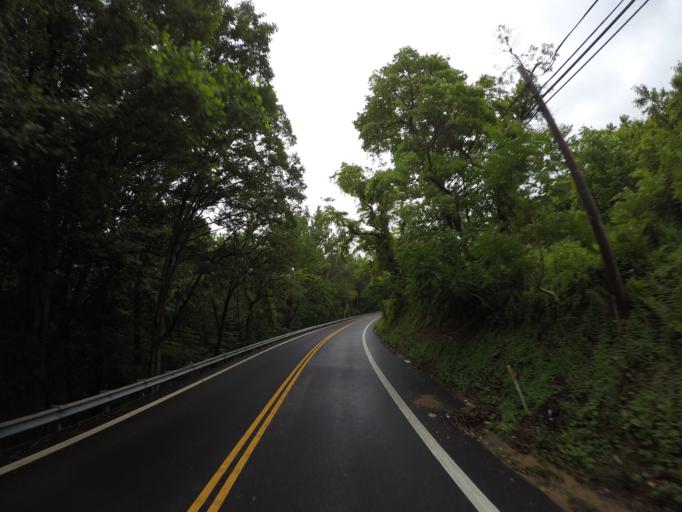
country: US
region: Maryland
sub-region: Washington County
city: Boonsboro
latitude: 39.4794
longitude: -77.6147
